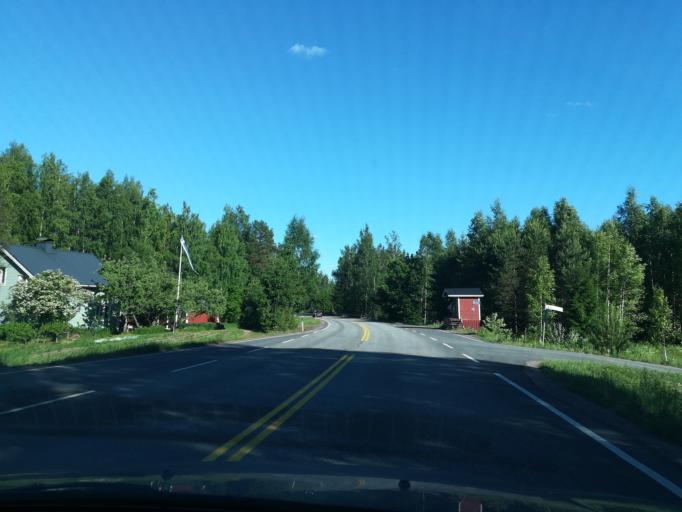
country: FI
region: South Karelia
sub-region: Imatra
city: Ruokolahti
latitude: 61.3537
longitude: 28.7230
